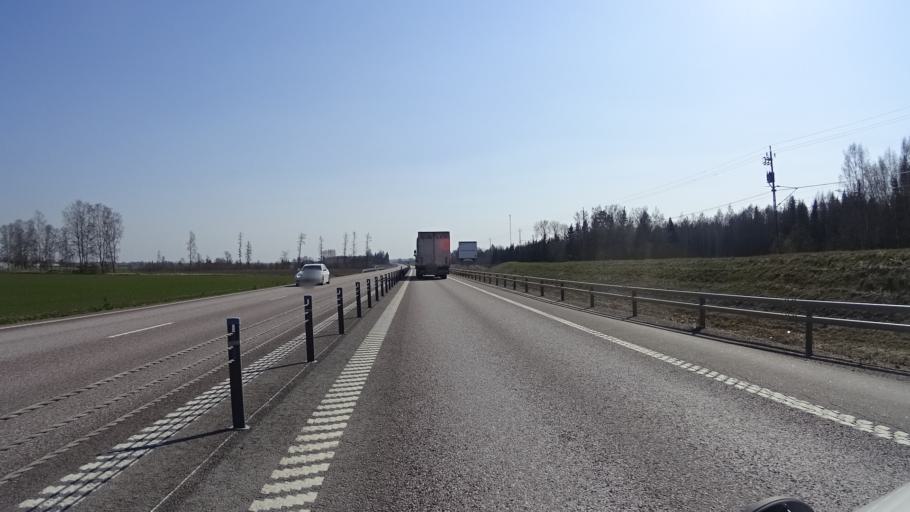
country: SE
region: OEstergoetland
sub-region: Motala Kommun
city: Stenstorp
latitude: 58.4211
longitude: 15.0710
